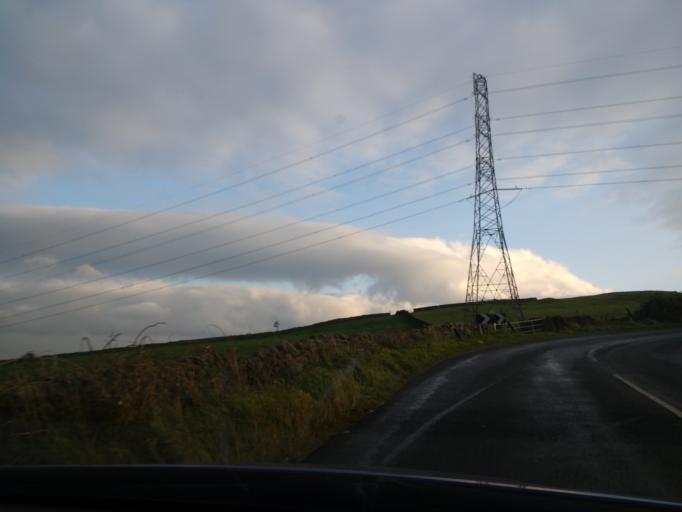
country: GB
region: England
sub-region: Lancashire
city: Lancaster
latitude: 54.0461
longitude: -2.7604
